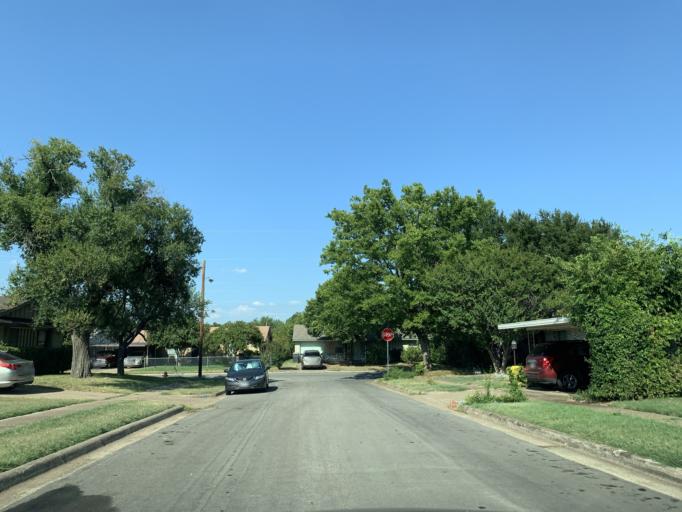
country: US
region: Texas
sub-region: Dallas County
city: Hutchins
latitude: 32.6591
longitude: -96.7683
